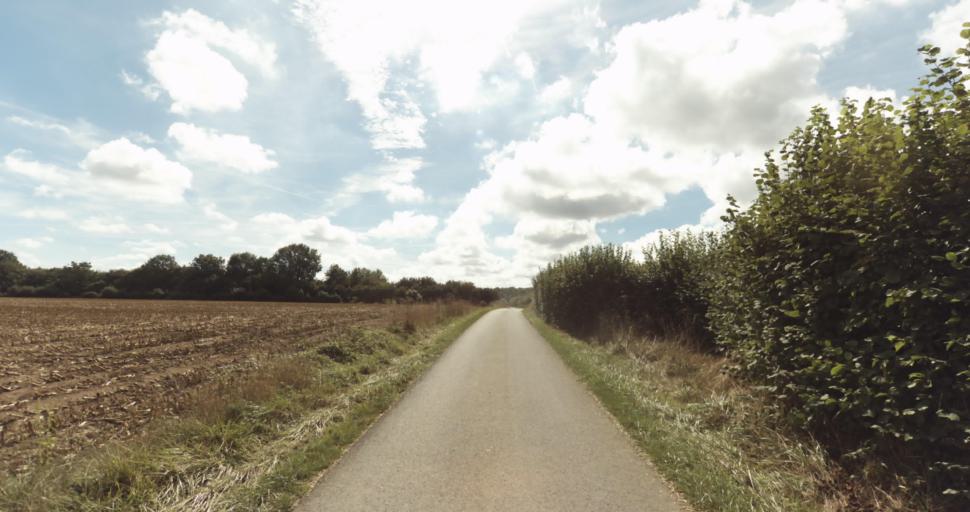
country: FR
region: Lower Normandy
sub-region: Departement de l'Orne
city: Vimoutiers
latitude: 48.9536
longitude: 0.3094
